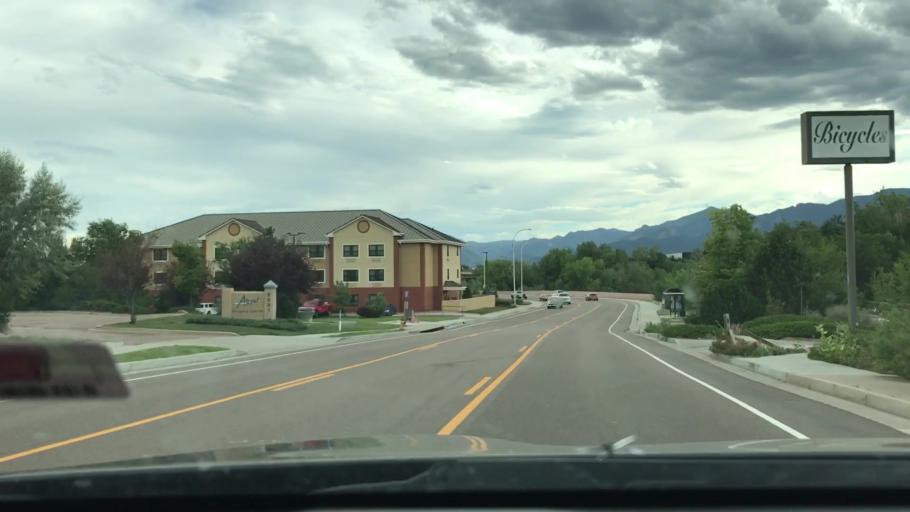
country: US
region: Colorado
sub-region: El Paso County
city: Colorado Springs
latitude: 38.9184
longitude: -104.8172
